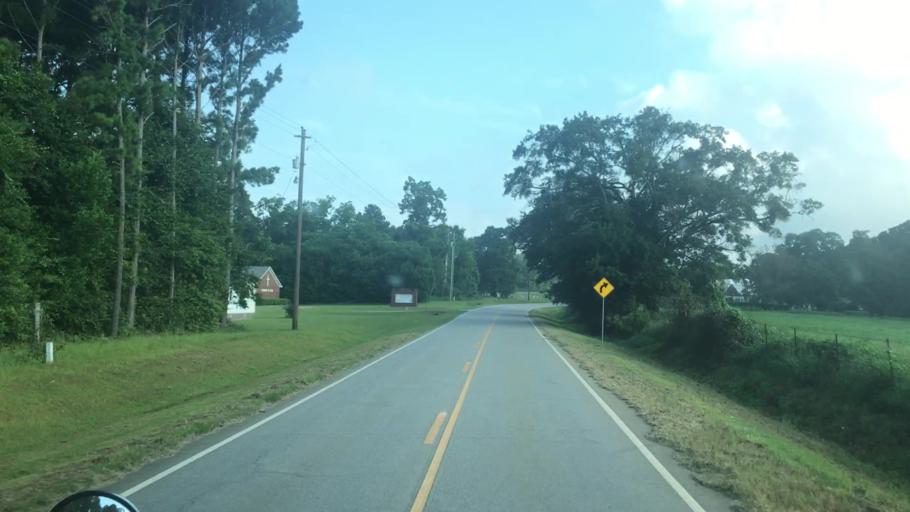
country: US
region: Florida
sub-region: Gadsden County
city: Havana
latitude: 30.7427
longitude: -84.4831
